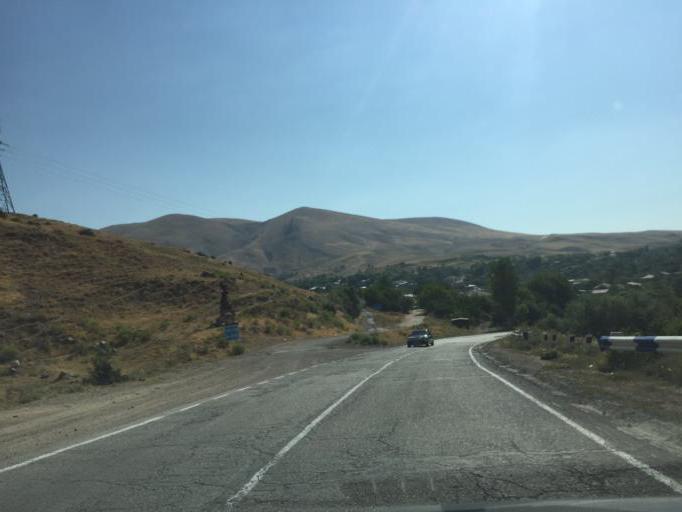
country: AM
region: Ararat
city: Zangakatun
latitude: 39.8180
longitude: 45.0293
